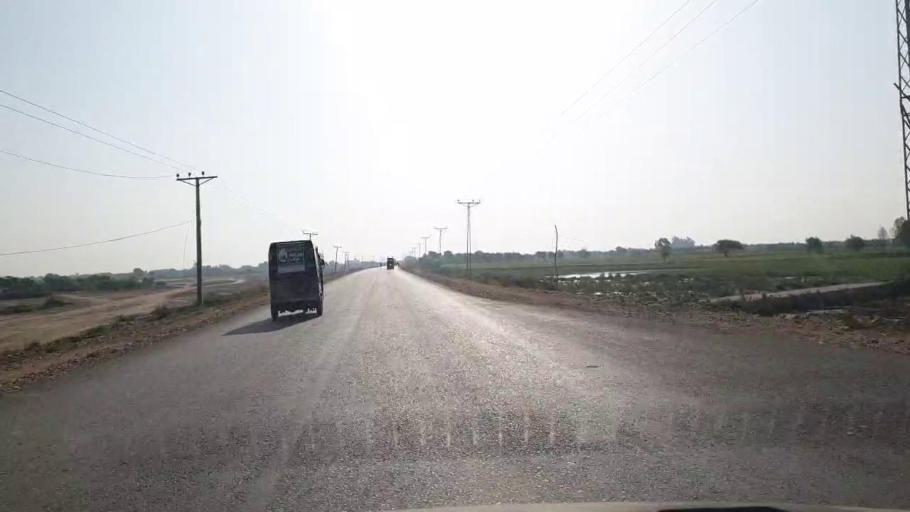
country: PK
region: Sindh
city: Badin
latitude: 24.6655
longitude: 68.8698
